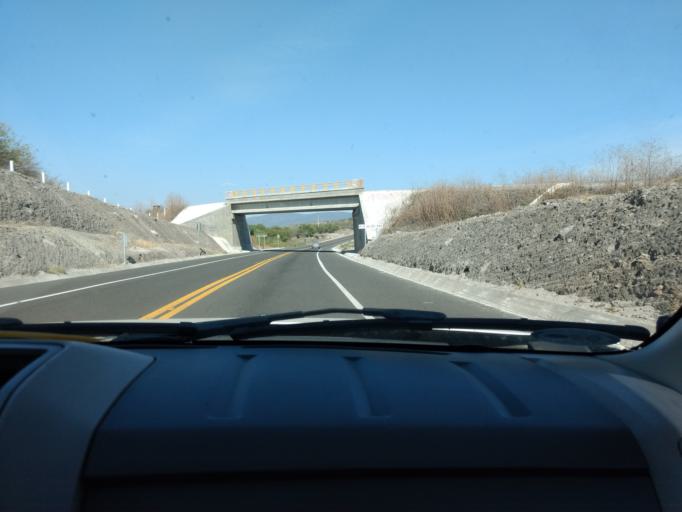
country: MX
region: Morelos
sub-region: Ayala
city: El Salitre
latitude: 18.6725
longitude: -98.9547
